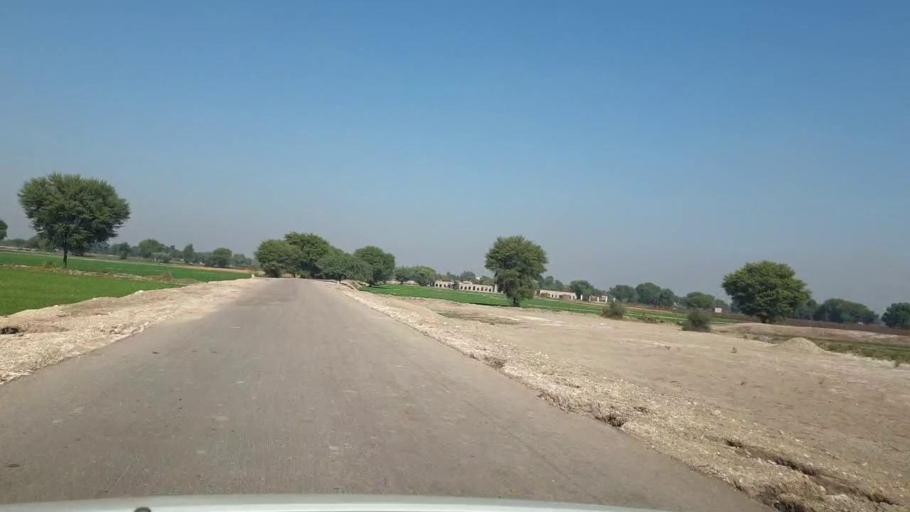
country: PK
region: Sindh
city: Johi
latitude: 26.6627
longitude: 67.7055
